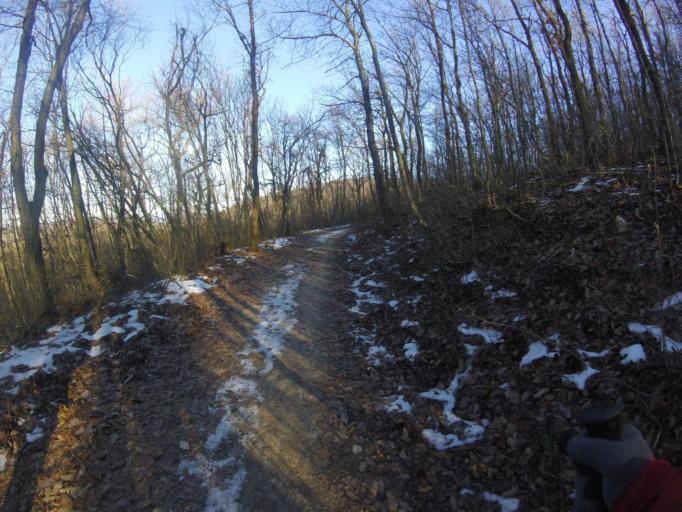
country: HU
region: Pest
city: Budakeszi
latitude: 47.5263
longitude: 18.9498
